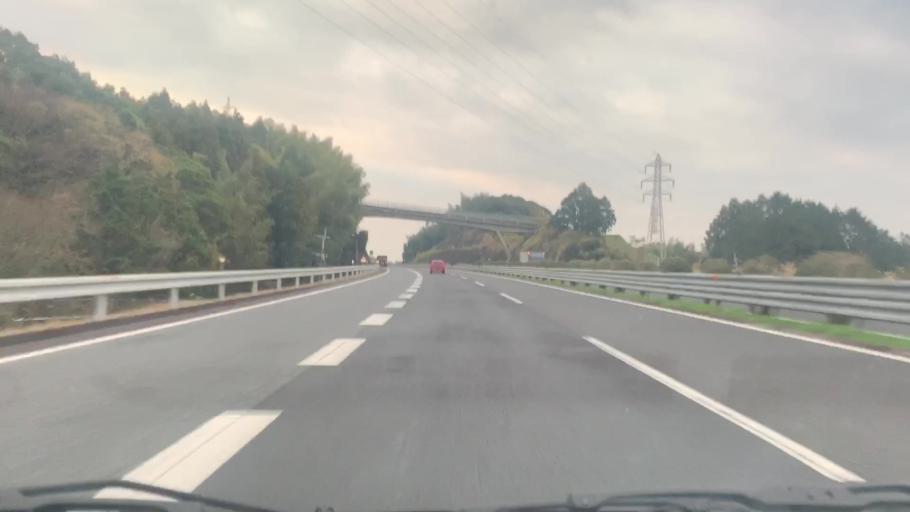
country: JP
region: Nagasaki
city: Omura
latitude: 32.9950
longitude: 129.9522
